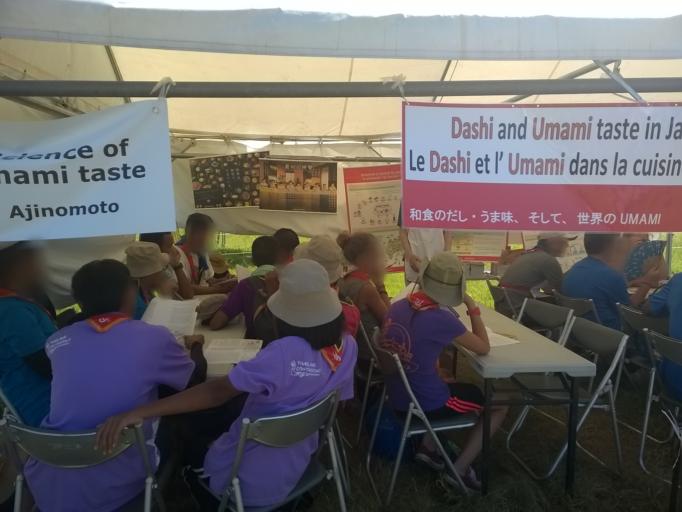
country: JP
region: Yamaguchi
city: Ogori-shimogo
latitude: 34.0164
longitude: 131.3698
